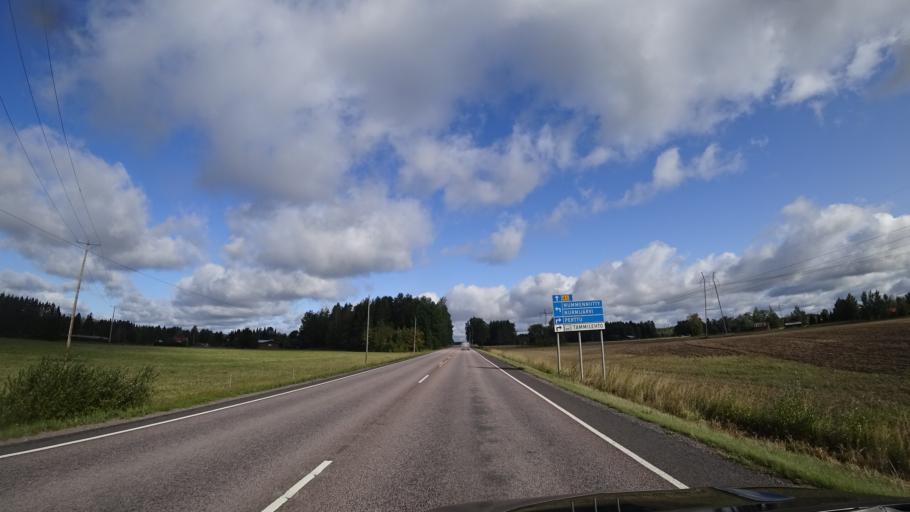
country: FI
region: Uusimaa
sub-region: Helsinki
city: Hyvinge
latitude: 60.5219
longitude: 24.9254
